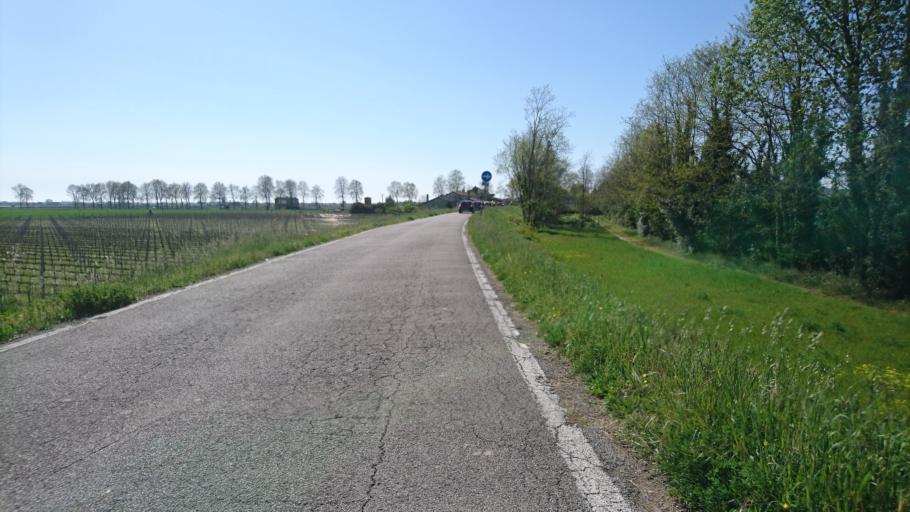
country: IT
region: Veneto
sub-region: Provincia di Venezia
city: Eraclea
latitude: 45.5728
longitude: 12.6781
